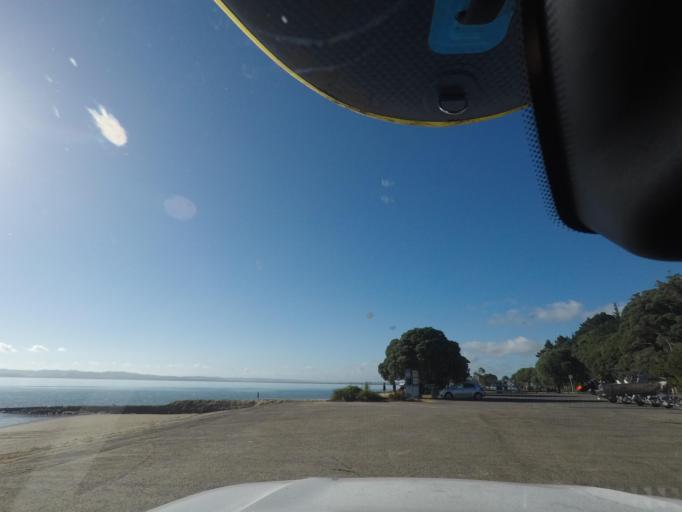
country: NZ
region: Auckland
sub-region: Auckland
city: Parakai
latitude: -36.5709
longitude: 174.3790
